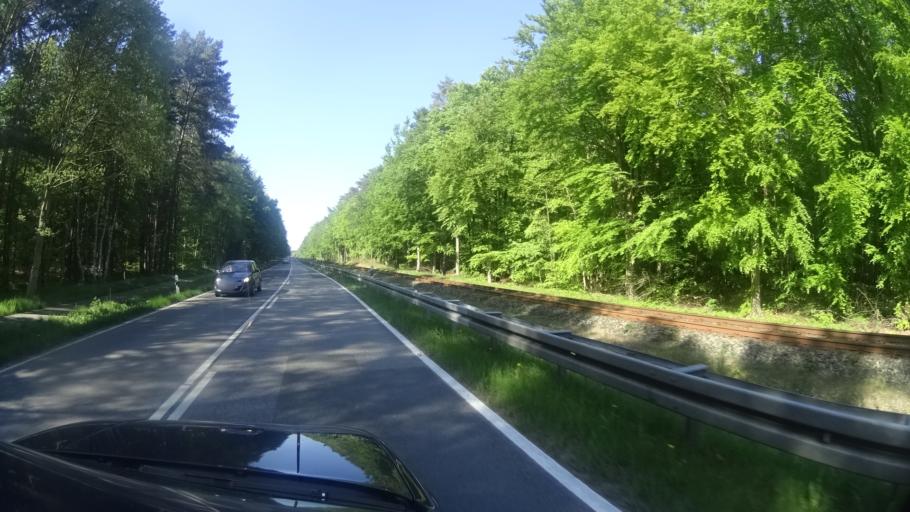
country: DE
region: Mecklenburg-Vorpommern
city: Seeheilbad Graal-Muritz
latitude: 54.2249
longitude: 12.2245
